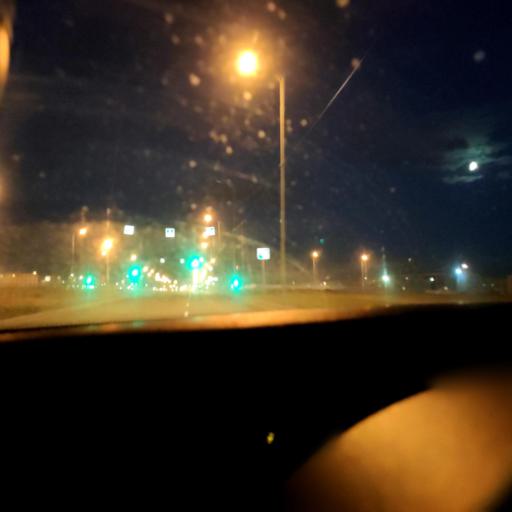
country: RU
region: Samara
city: Petra-Dubrava
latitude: 53.2995
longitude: 50.3178
